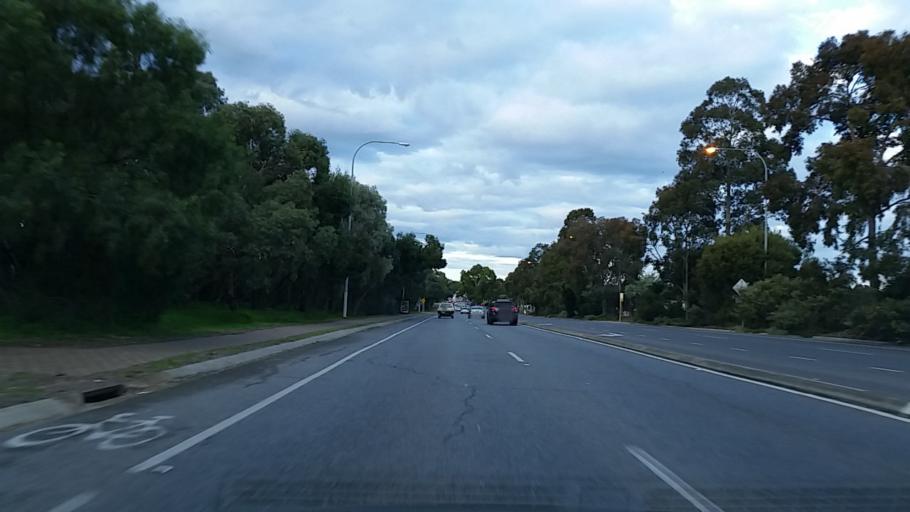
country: AU
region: South Australia
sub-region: Salisbury
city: Ingle Farm
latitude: -34.8243
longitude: 138.6279
